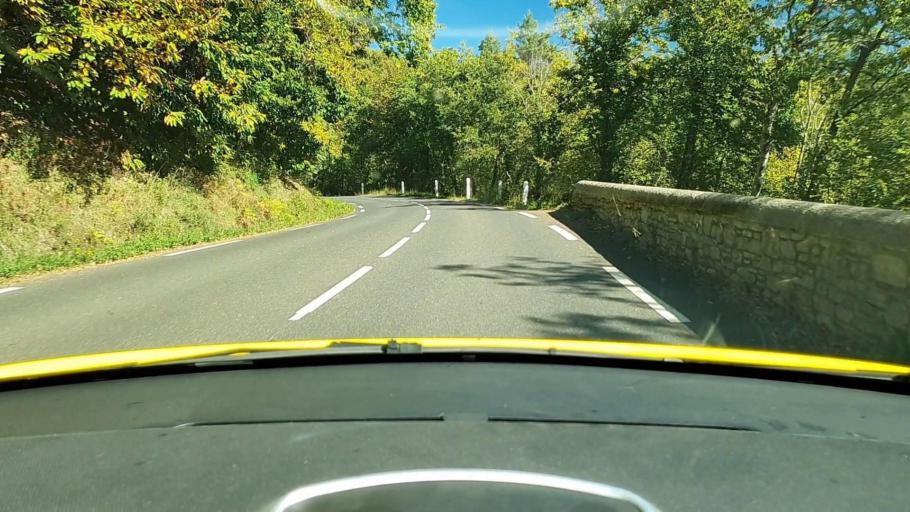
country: FR
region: Languedoc-Roussillon
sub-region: Departement du Gard
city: Le Vigan
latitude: 43.9702
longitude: 3.4076
